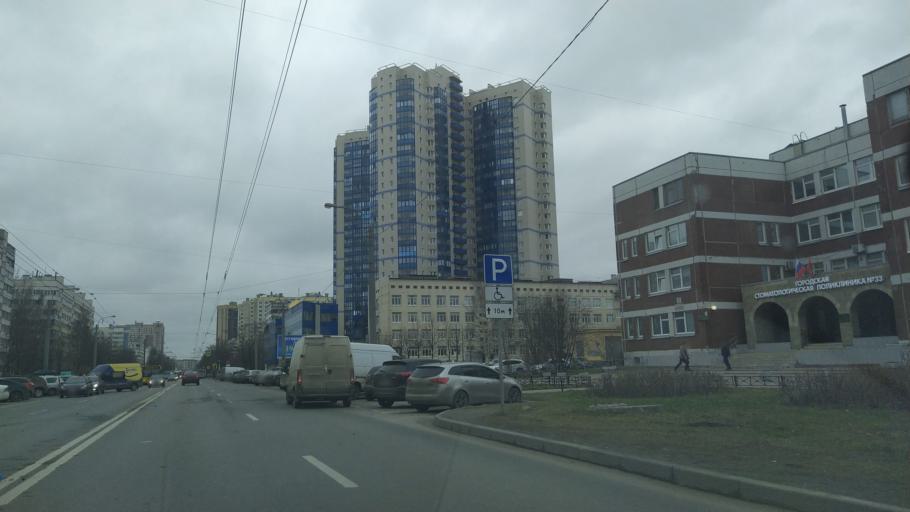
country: RU
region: St.-Petersburg
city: Kolomyagi
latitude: 60.0096
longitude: 30.2939
